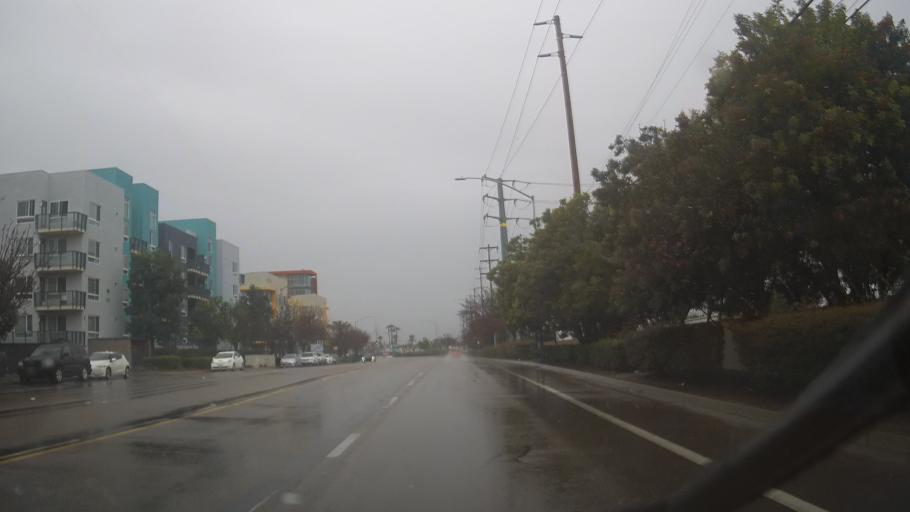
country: US
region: California
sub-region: San Diego County
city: San Diego
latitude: 32.8291
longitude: -117.1376
